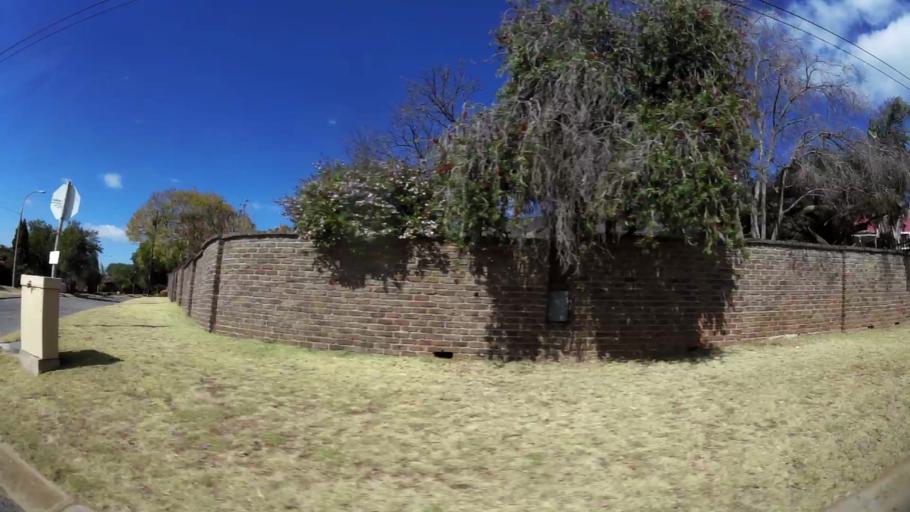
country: ZA
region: Gauteng
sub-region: City of Johannesburg Metropolitan Municipality
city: Roodepoort
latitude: -26.1175
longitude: 27.8397
